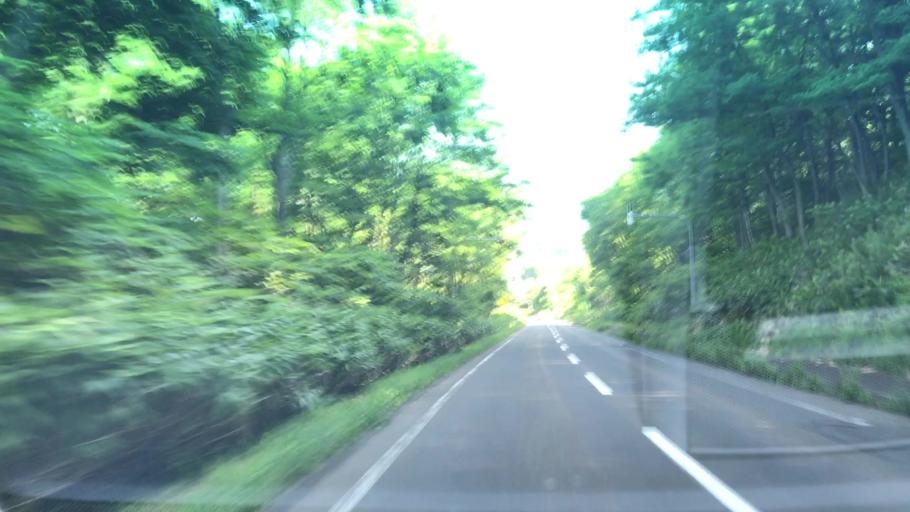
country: JP
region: Hokkaido
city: Yoichi
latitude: 43.0627
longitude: 140.7131
